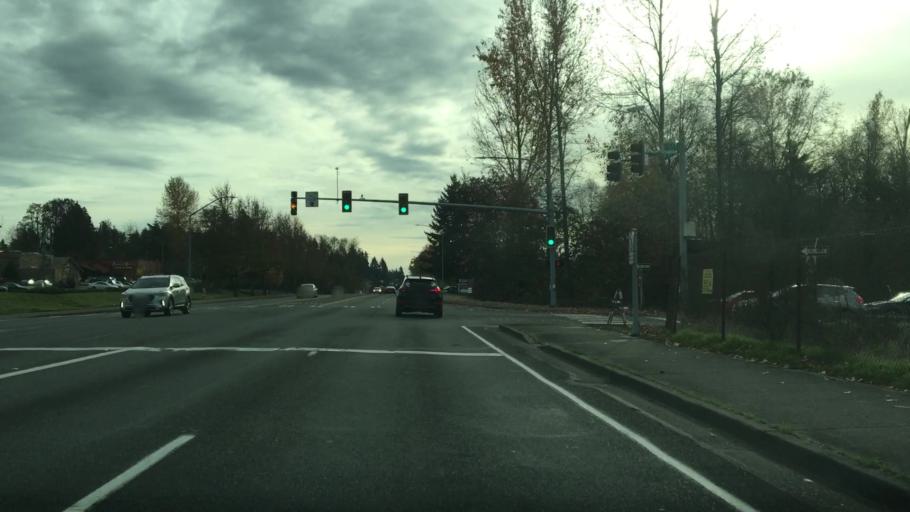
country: US
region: Washington
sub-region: Pierce County
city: Puyallup
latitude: 47.1582
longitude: -122.3041
